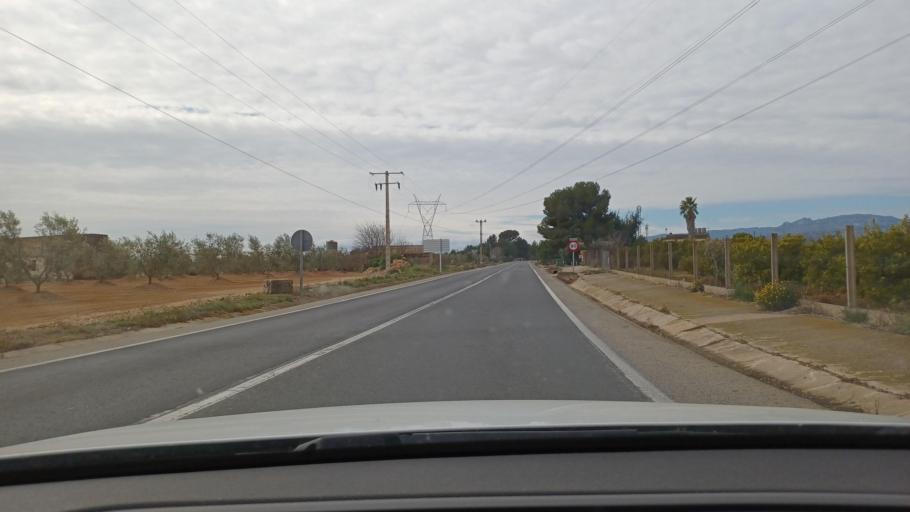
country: ES
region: Catalonia
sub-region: Provincia de Tarragona
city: Santa Barbara
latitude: 40.7068
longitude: 0.5027
